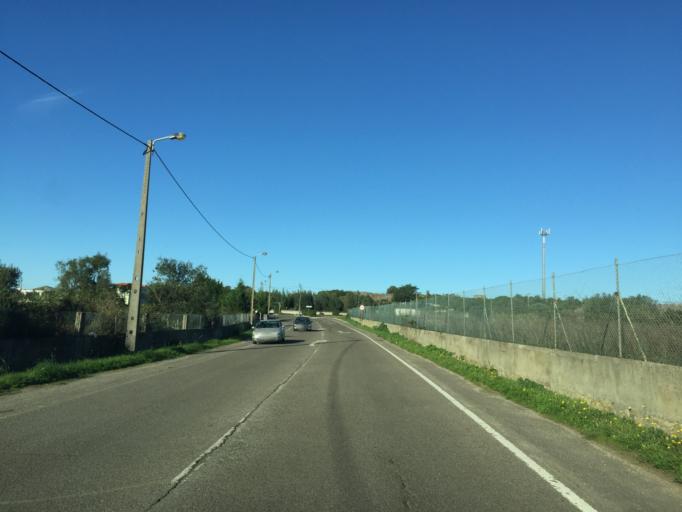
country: PT
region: Lisbon
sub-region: Sintra
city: Pero Pinheiro
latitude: 38.8605
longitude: -9.3176
